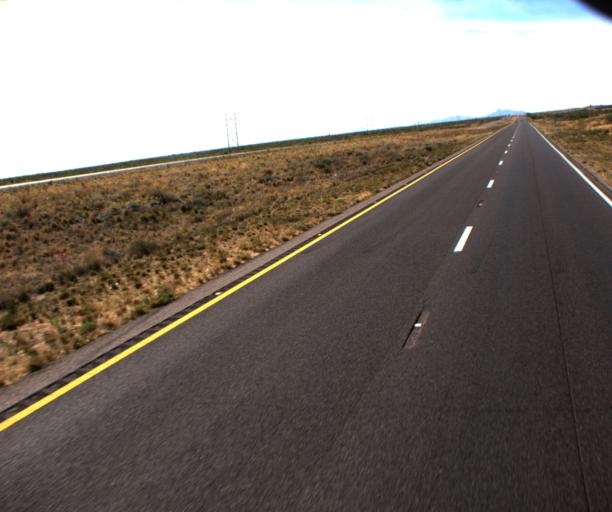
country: US
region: Arizona
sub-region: Graham County
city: Swift Trail Junction
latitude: 32.5507
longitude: -109.6779
